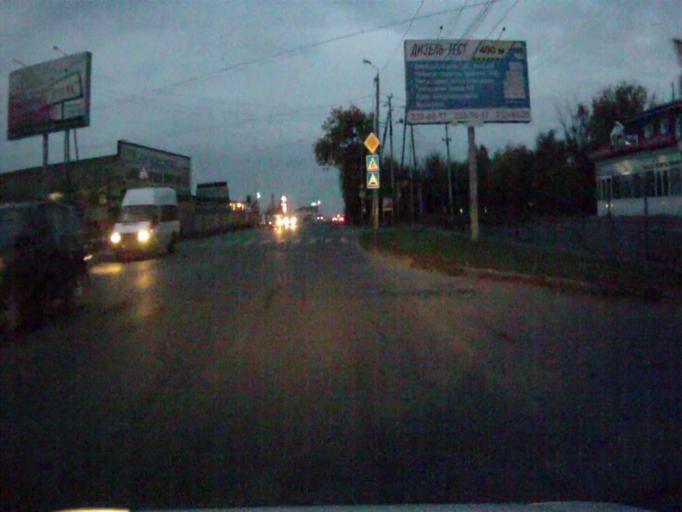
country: RU
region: Chelyabinsk
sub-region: Gorod Chelyabinsk
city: Chelyabinsk
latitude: 55.1519
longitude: 61.3037
